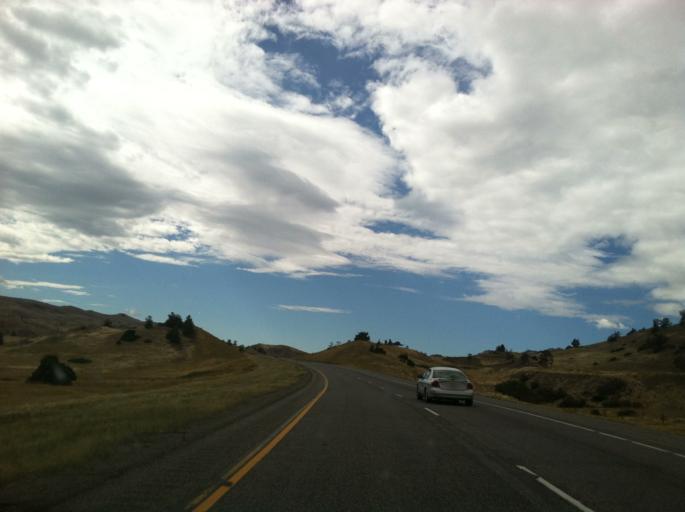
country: US
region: Montana
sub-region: Park County
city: Livingston
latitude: 45.6613
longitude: -110.6578
